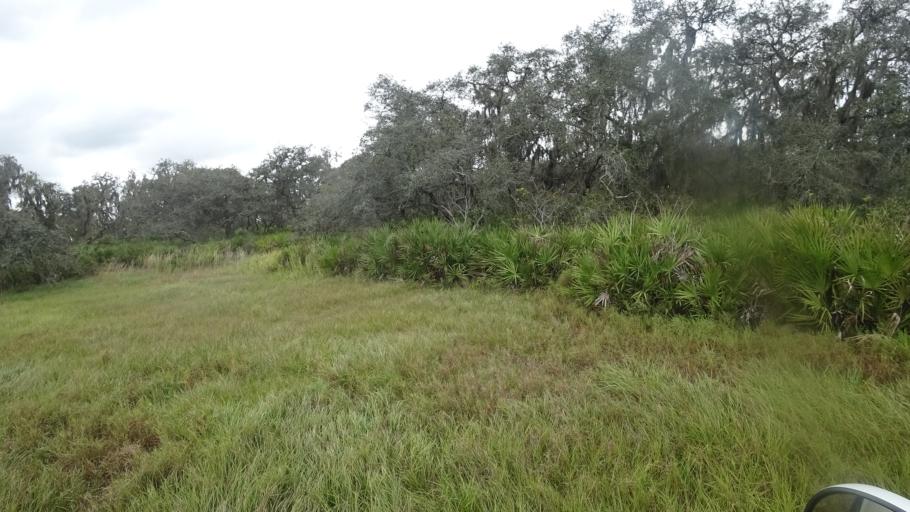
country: US
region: Florida
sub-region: Hillsborough County
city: Wimauma
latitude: 27.5610
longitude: -82.1342
